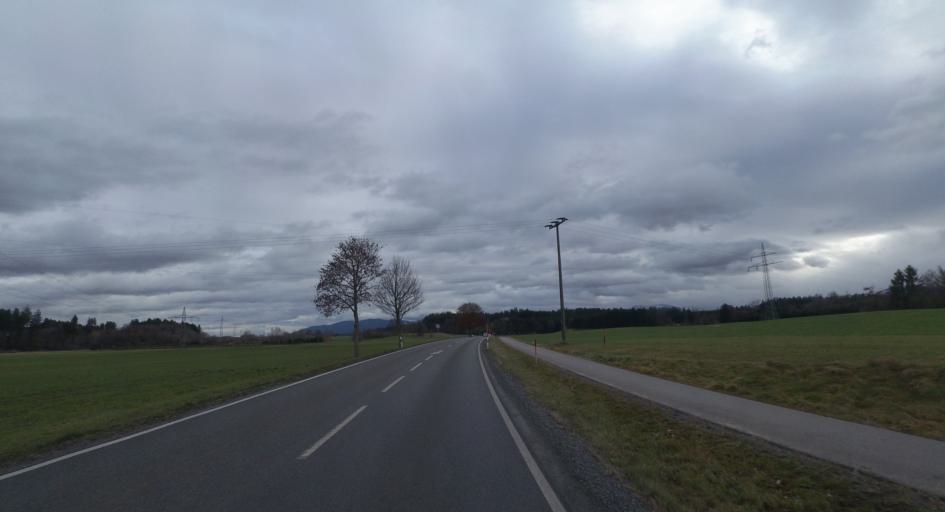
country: DE
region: Bavaria
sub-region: Upper Bavaria
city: Vachendorf
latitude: 47.8748
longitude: 12.5985
